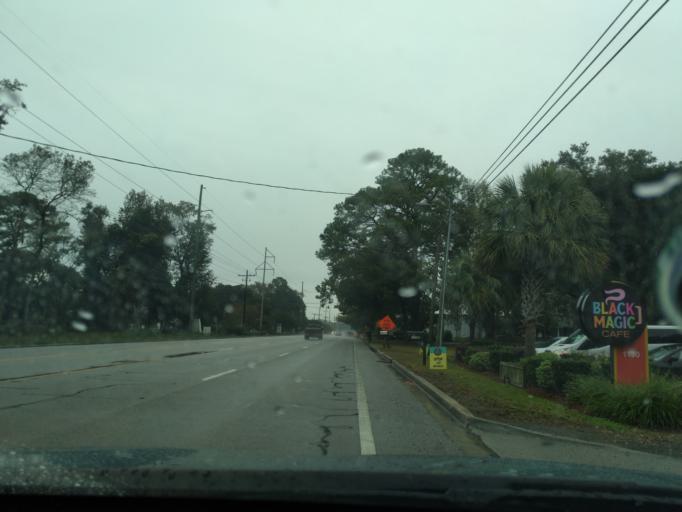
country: US
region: South Carolina
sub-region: Charleston County
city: Charleston
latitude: 32.7253
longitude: -79.9675
